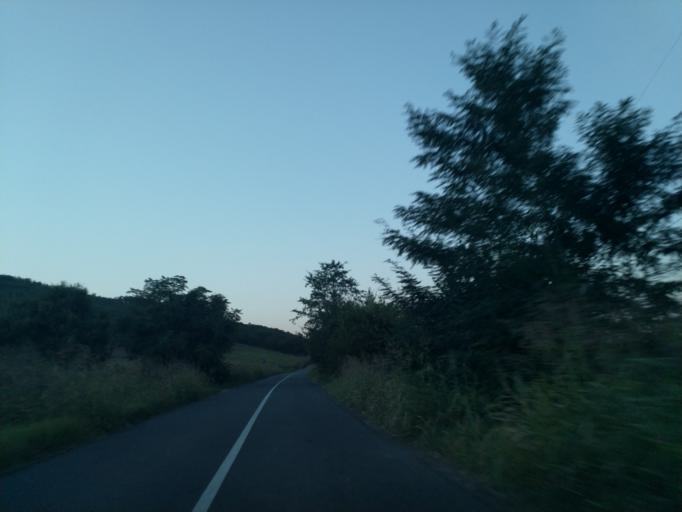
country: RS
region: Central Serbia
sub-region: Rasinski Okrug
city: Krusevac
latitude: 43.6403
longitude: 21.3735
